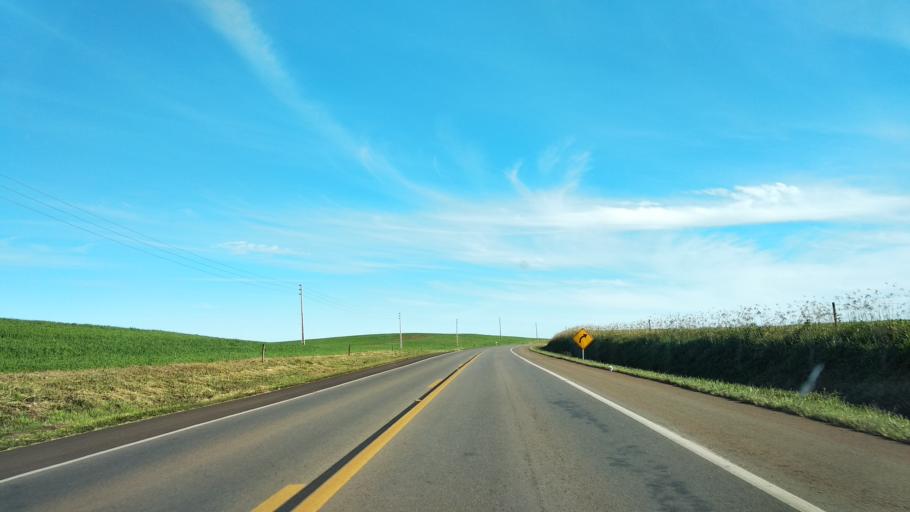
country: BR
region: Santa Catarina
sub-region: Celso Ramos
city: Celso Ramos
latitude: -27.5198
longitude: -51.3515
